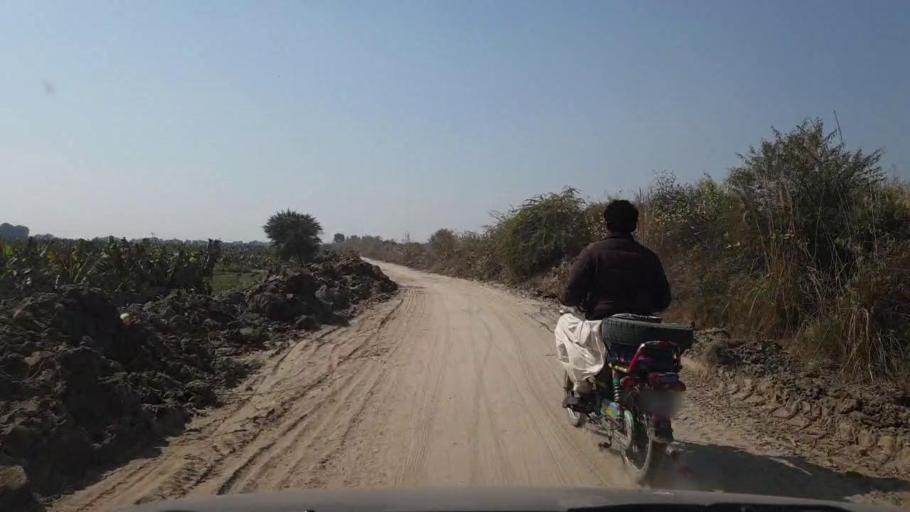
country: PK
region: Sindh
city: Tando Allahyar
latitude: 25.4354
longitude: 68.6427
